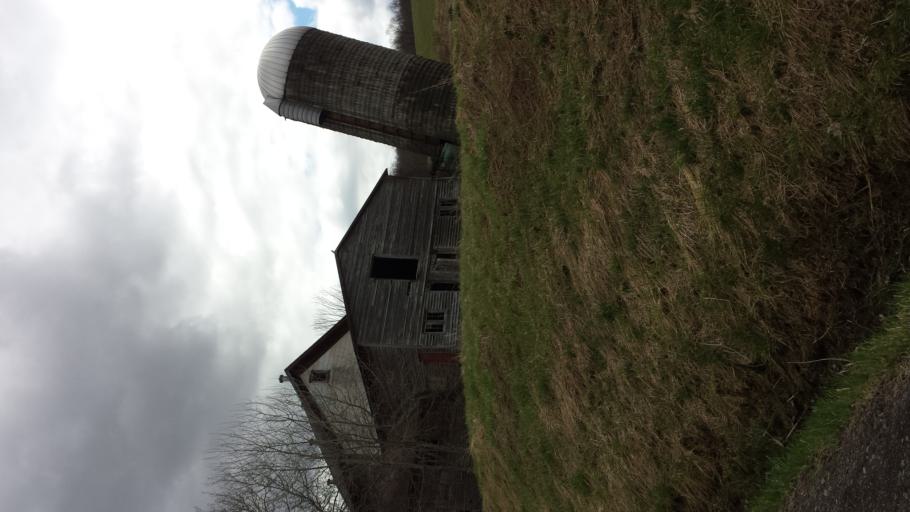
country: US
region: New York
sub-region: Otsego County
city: Oneonta
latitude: 42.3470
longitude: -75.0292
